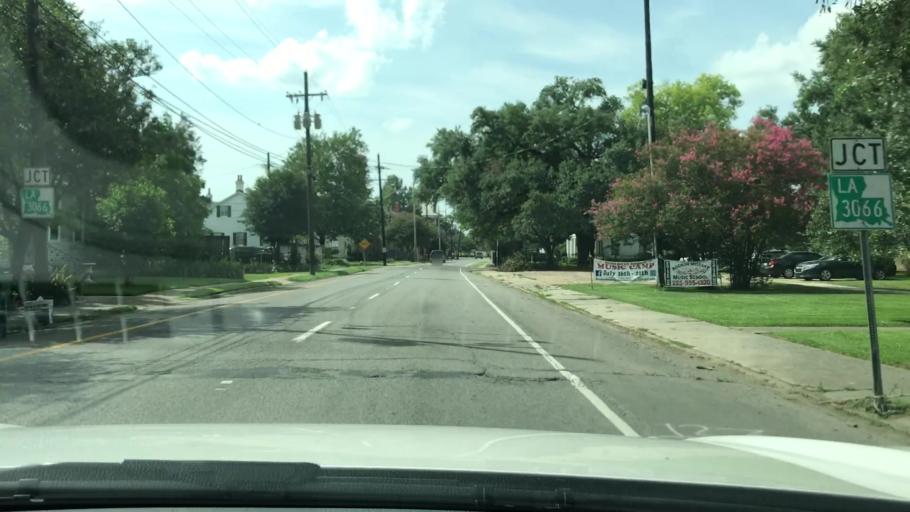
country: US
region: Louisiana
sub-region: Iberville Parish
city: Plaquemine
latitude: 30.2893
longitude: -91.2330
